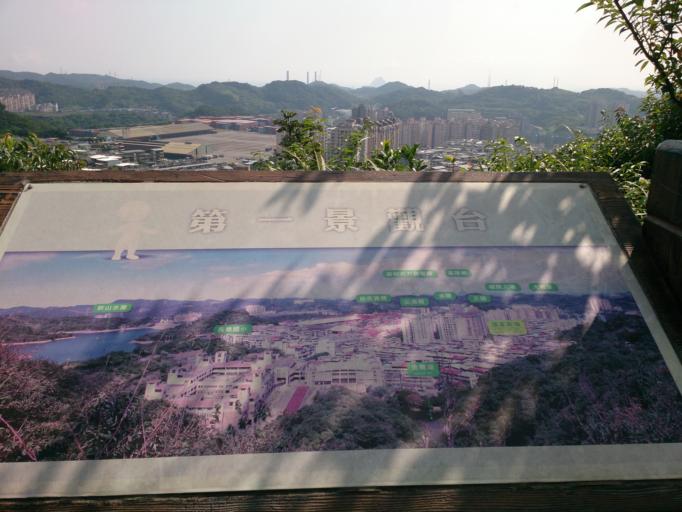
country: TW
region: Taiwan
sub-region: Keelung
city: Keelung
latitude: 25.1232
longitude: 121.7105
